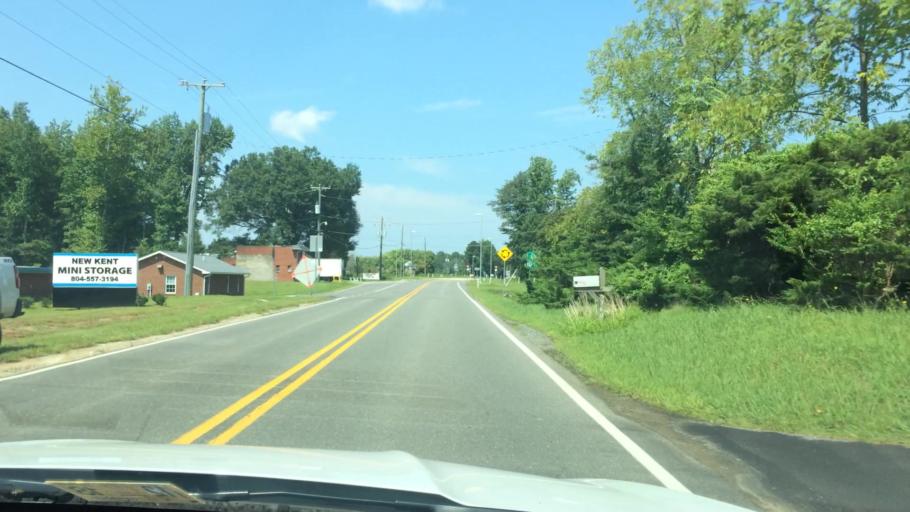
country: US
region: Virginia
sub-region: New Kent County
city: New Kent
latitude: 37.5322
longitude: -77.1129
